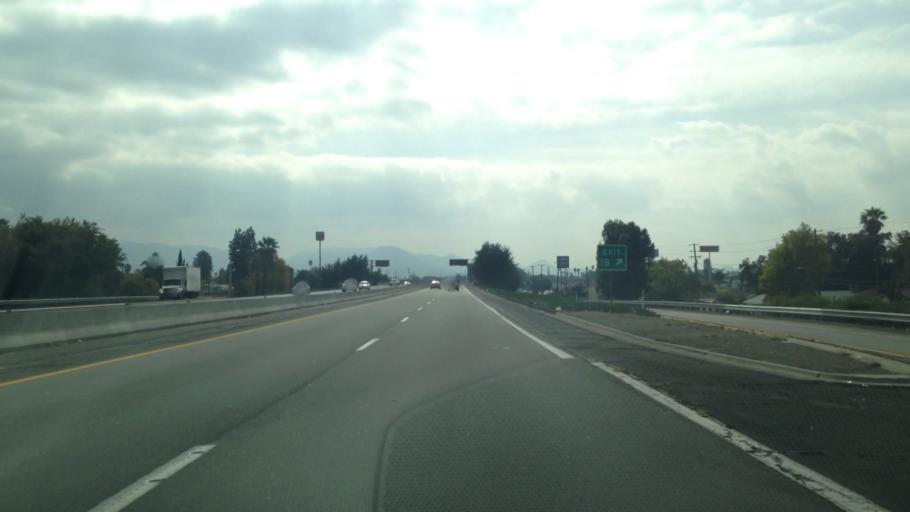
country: US
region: California
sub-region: San Bernardino County
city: San Bernardino
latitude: 34.1390
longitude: -117.3027
